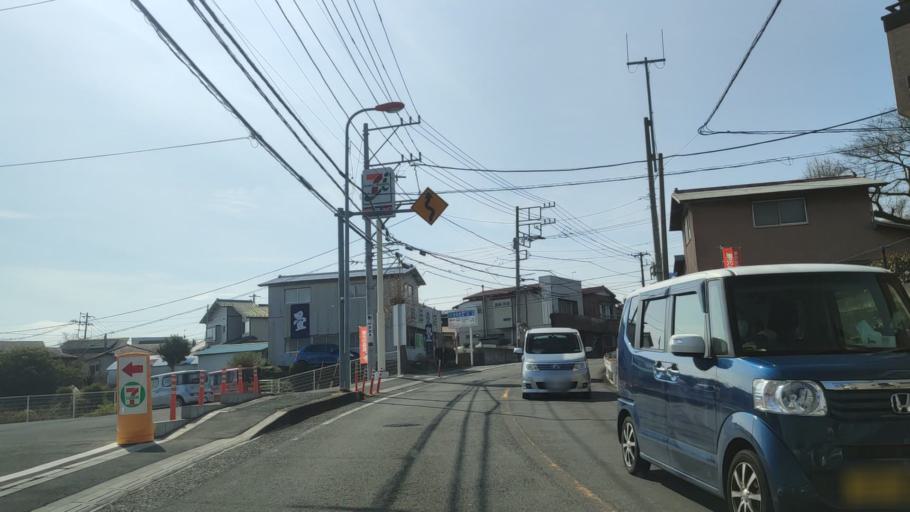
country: JP
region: Kanagawa
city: Isehara
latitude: 35.3869
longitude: 139.2809
